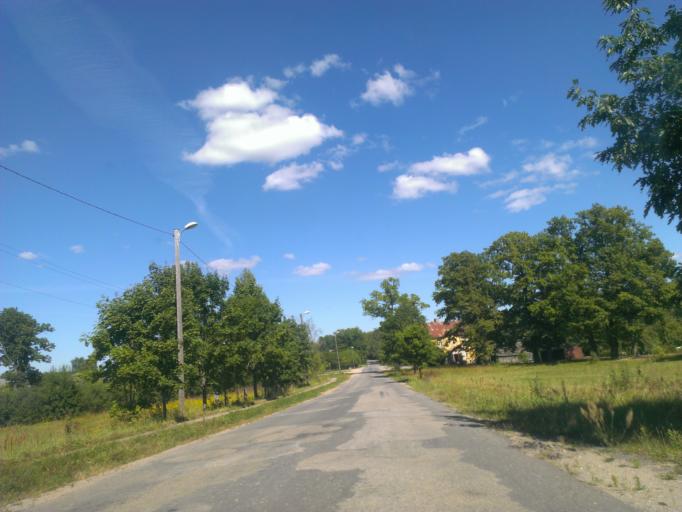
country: LV
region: Malpils
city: Malpils
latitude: 57.0056
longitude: 24.9610
